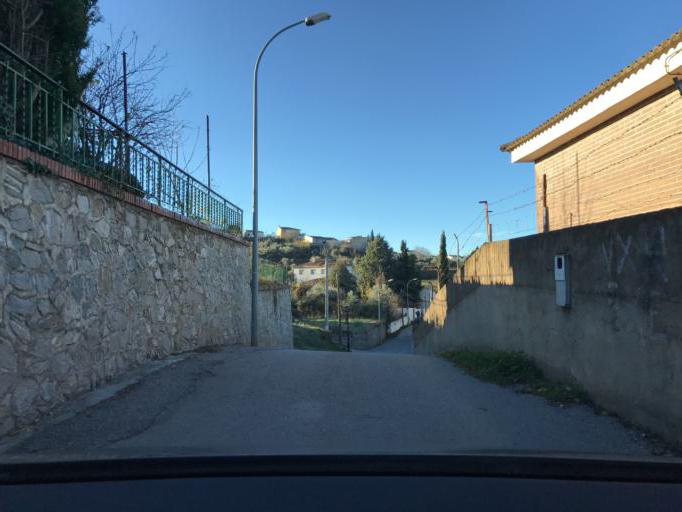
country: ES
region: Andalusia
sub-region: Provincia de Granada
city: Nivar
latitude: 37.2617
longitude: -3.5744
